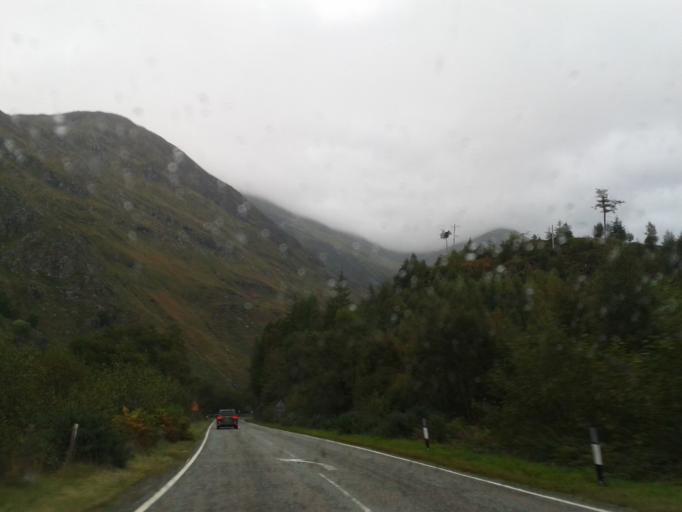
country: GB
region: Scotland
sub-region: Highland
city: Fort William
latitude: 57.2058
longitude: -5.4007
